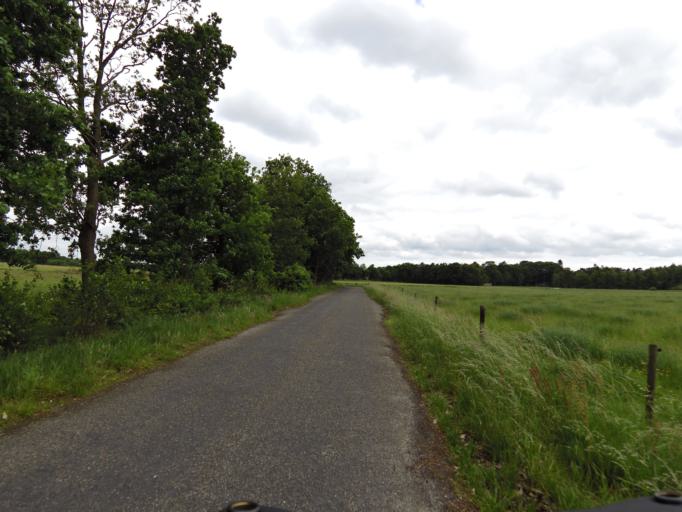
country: NL
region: North Brabant
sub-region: Gemeente Breda
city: Breda
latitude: 51.5351
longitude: 4.8661
